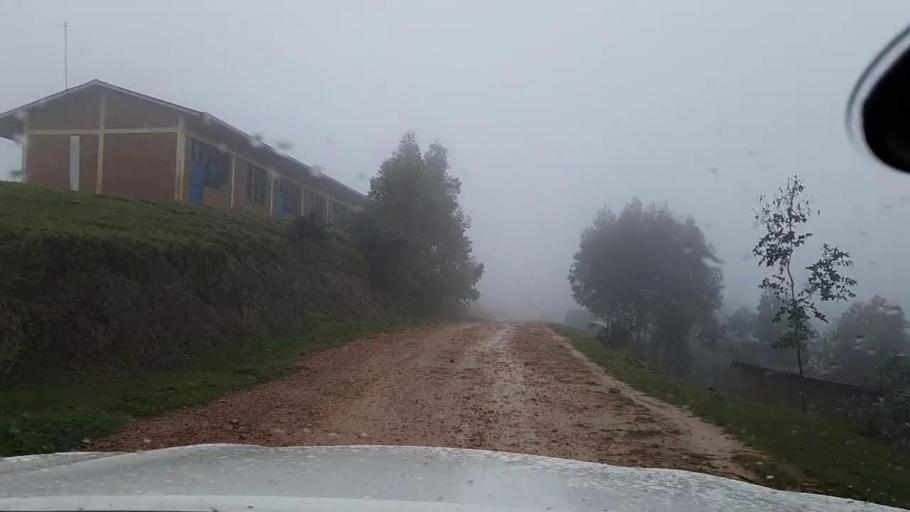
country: RW
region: Western Province
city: Kibuye
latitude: -2.1370
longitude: 29.4676
